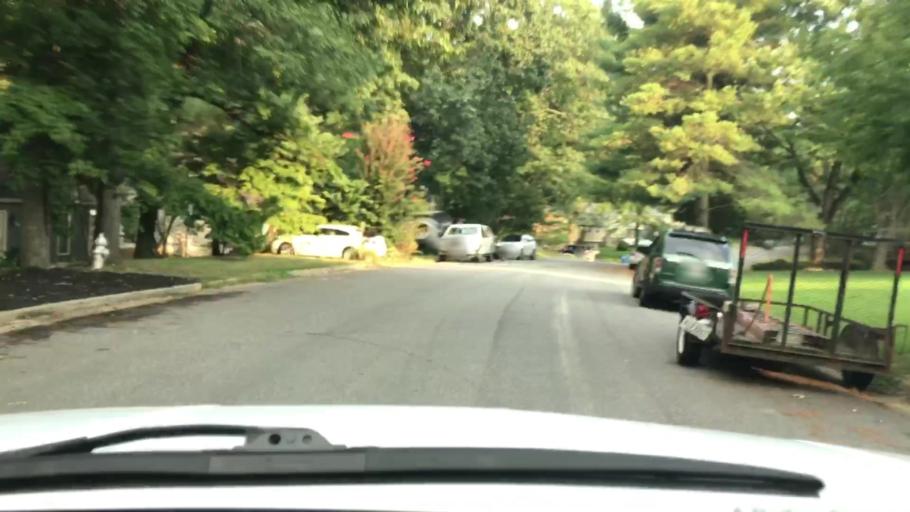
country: US
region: Virginia
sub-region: Chesterfield County
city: Chesterfield
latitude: 37.4414
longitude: -77.5161
